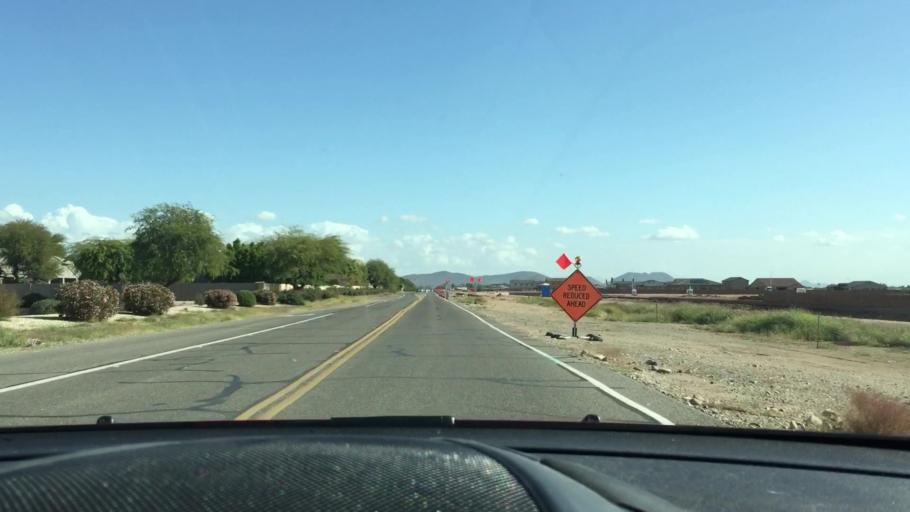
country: US
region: Arizona
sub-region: Maricopa County
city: Sun City West
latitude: 33.6962
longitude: -112.2679
